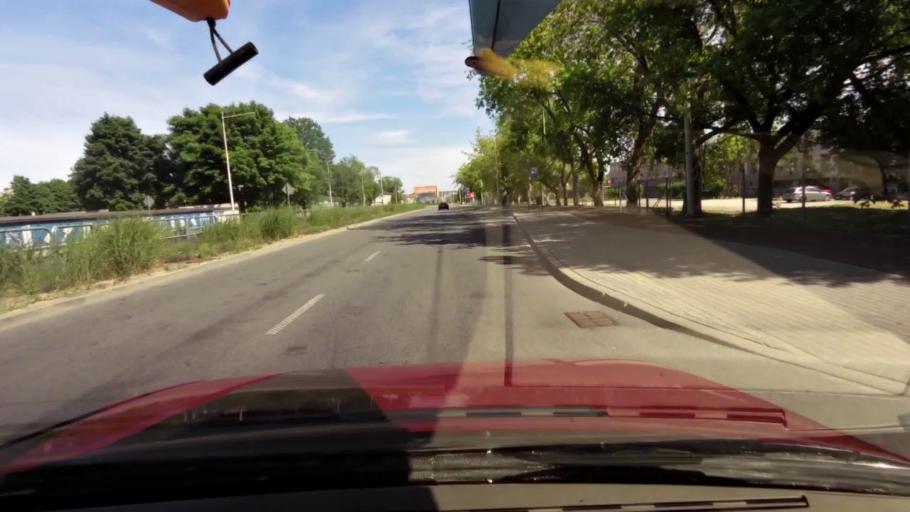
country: PL
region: Pomeranian Voivodeship
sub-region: Powiat slupski
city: Kobylnica
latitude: 54.4560
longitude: 17.0044
